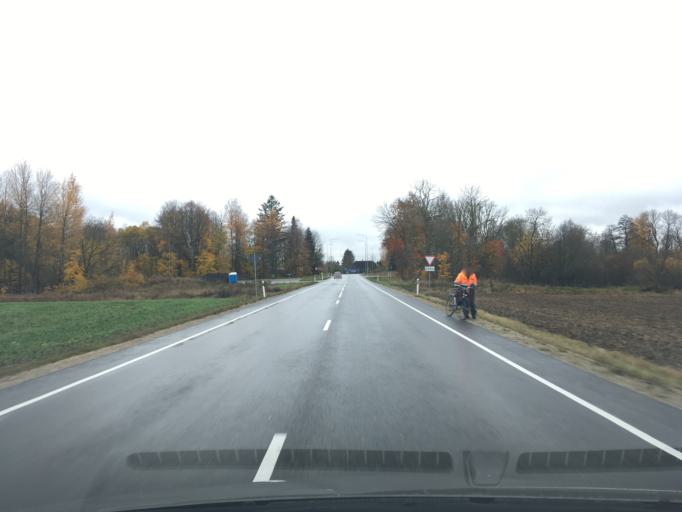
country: EE
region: Jogevamaa
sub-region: Tabivere vald
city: Tabivere
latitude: 58.4322
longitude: 26.4871
